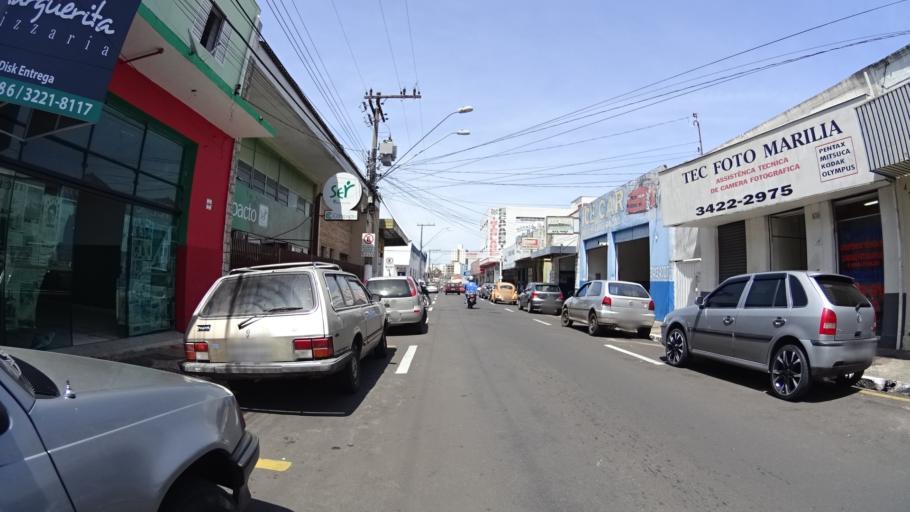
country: BR
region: Sao Paulo
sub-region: Marilia
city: Marilia
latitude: -22.2208
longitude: -49.9527
